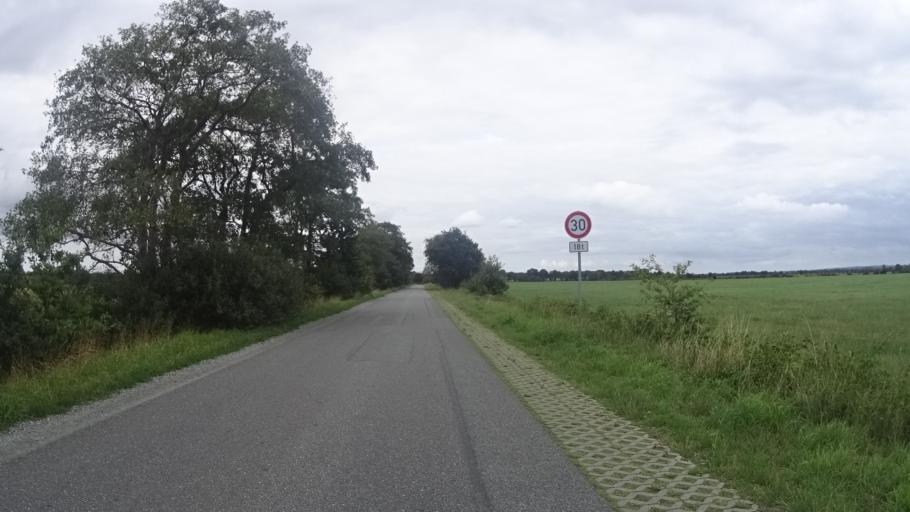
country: DE
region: Lower Saxony
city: Stinstedt
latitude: 53.6447
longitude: 8.9601
